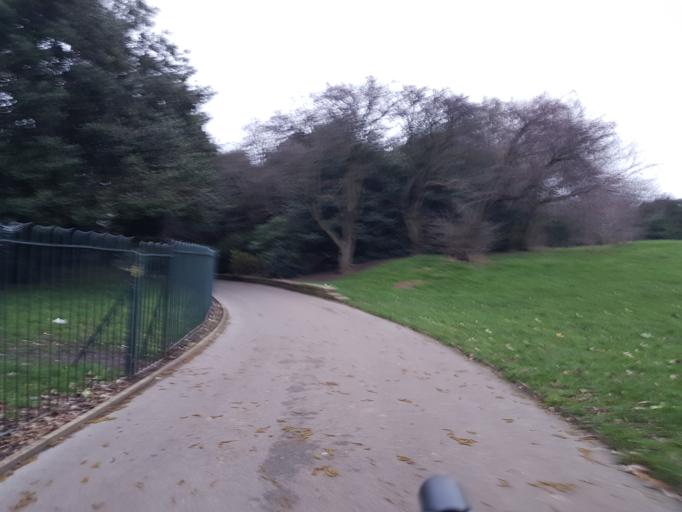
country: GB
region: England
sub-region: Liverpool
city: Liverpool
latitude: 53.4358
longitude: -2.9658
